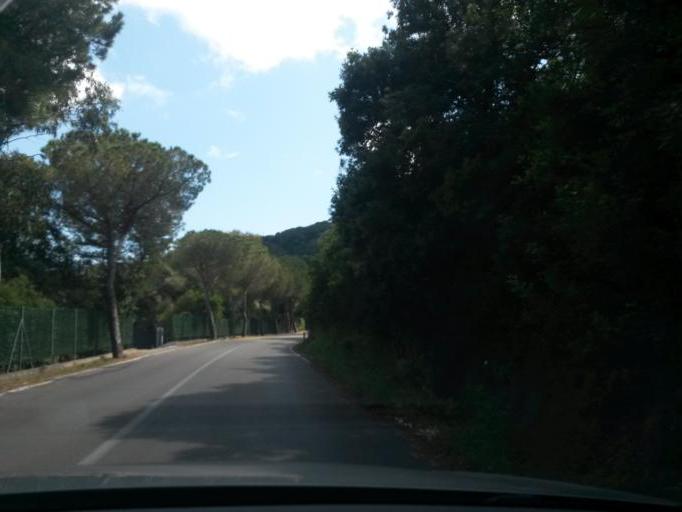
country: IT
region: Tuscany
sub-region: Provincia di Livorno
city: Marciana Marina
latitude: 42.7965
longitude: 10.2159
